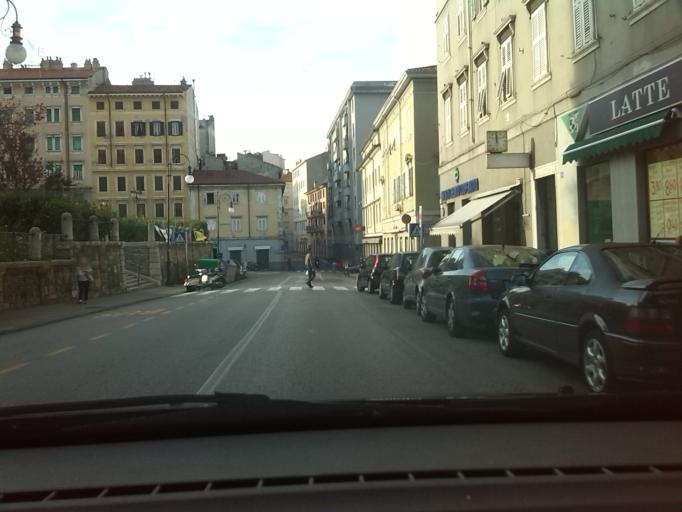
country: IT
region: Friuli Venezia Giulia
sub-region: Provincia di Trieste
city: Trieste
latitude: 45.6429
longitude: 13.7801
